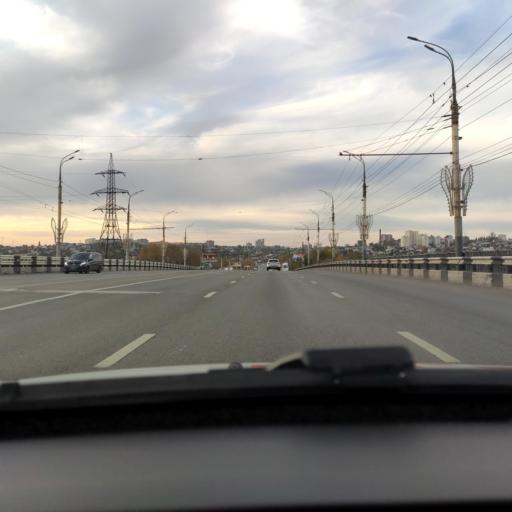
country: RU
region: Voronezj
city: Voronezh
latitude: 51.6338
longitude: 39.2232
